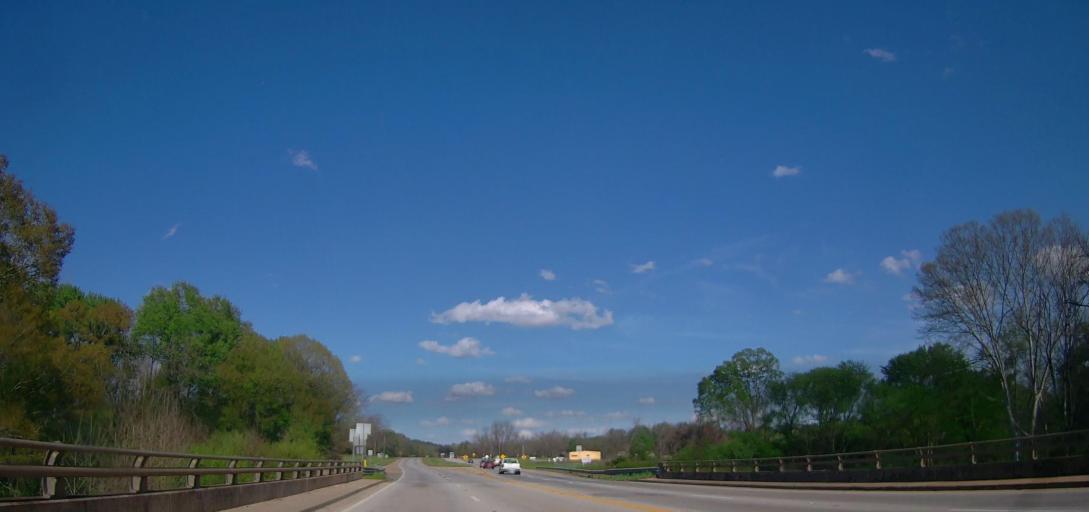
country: US
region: Georgia
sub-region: Baldwin County
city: Hardwick
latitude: 33.0840
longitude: -83.2139
